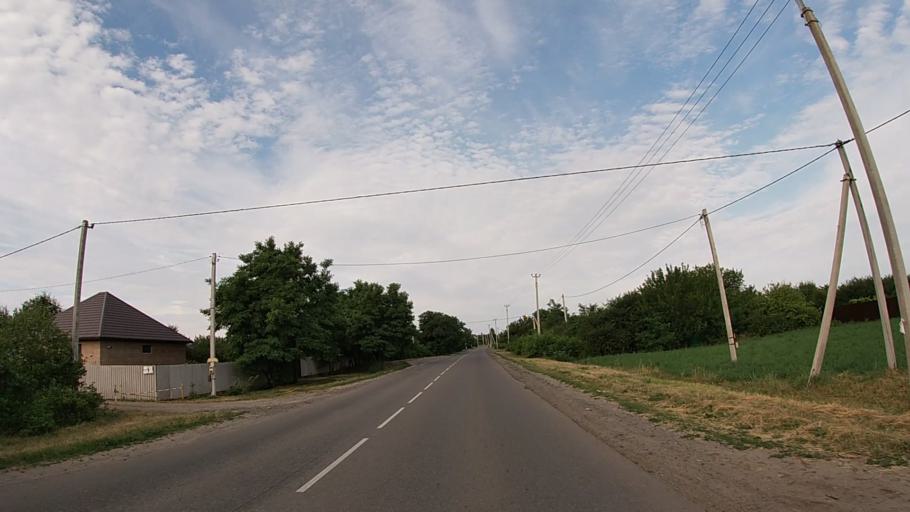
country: RU
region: Belgorod
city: Severnyy
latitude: 50.6957
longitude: 36.5726
